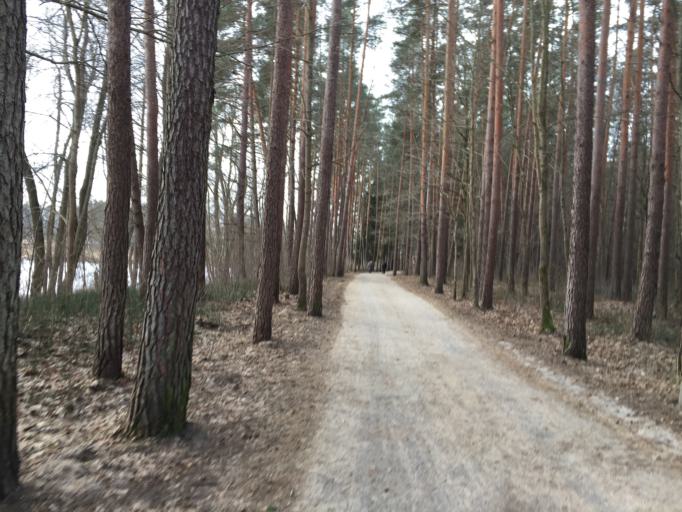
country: LV
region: Valmieras Rajons
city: Valmiera
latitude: 57.5337
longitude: 25.4401
